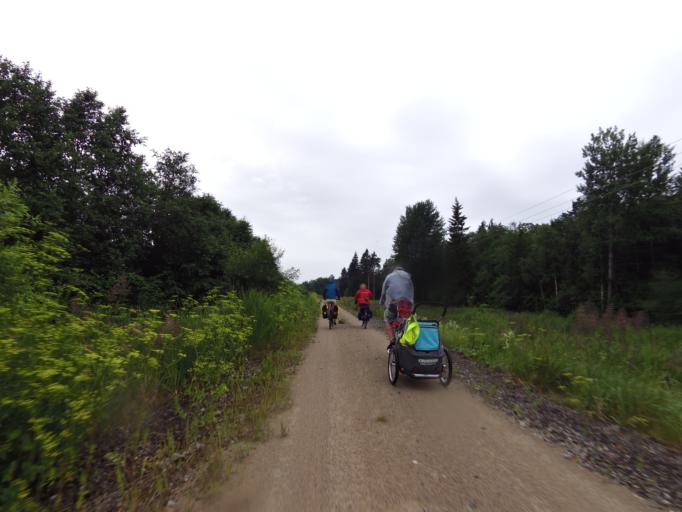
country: EE
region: Harju
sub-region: Nissi vald
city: Turba
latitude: 58.9924
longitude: 23.9569
